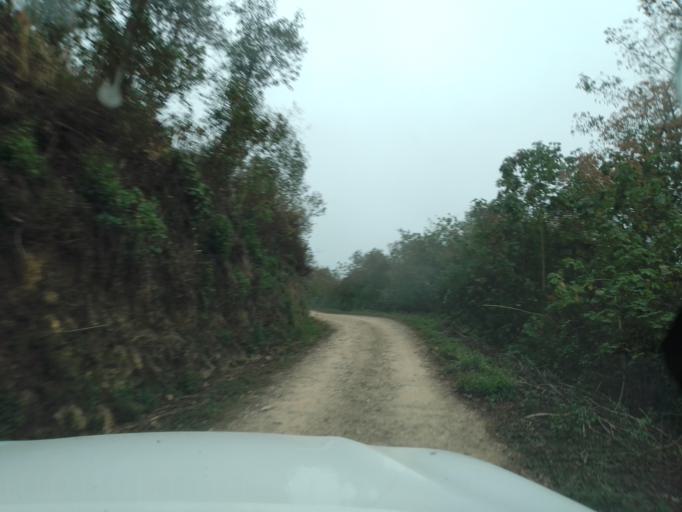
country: MX
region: Chiapas
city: Motozintla de Mendoza
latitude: 15.2149
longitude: -92.2201
